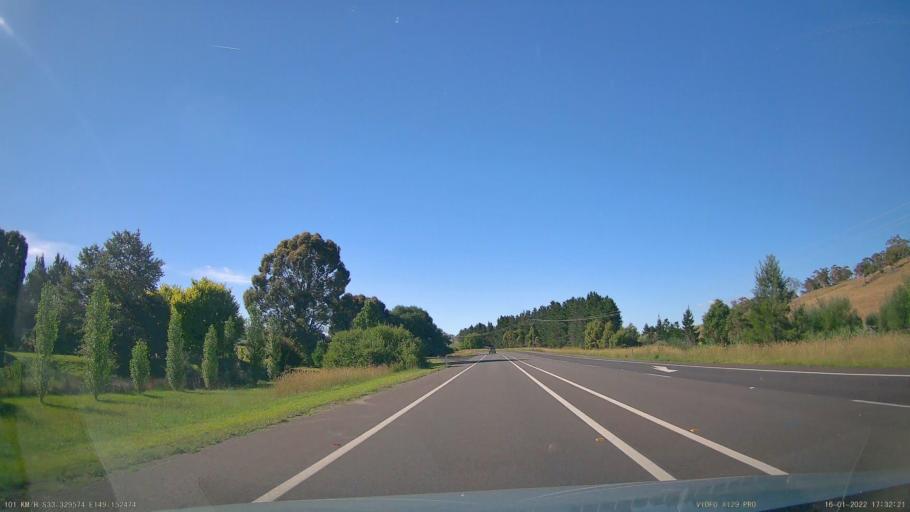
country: AU
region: New South Wales
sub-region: Orange Municipality
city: Orange
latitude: -33.3293
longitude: 149.1524
